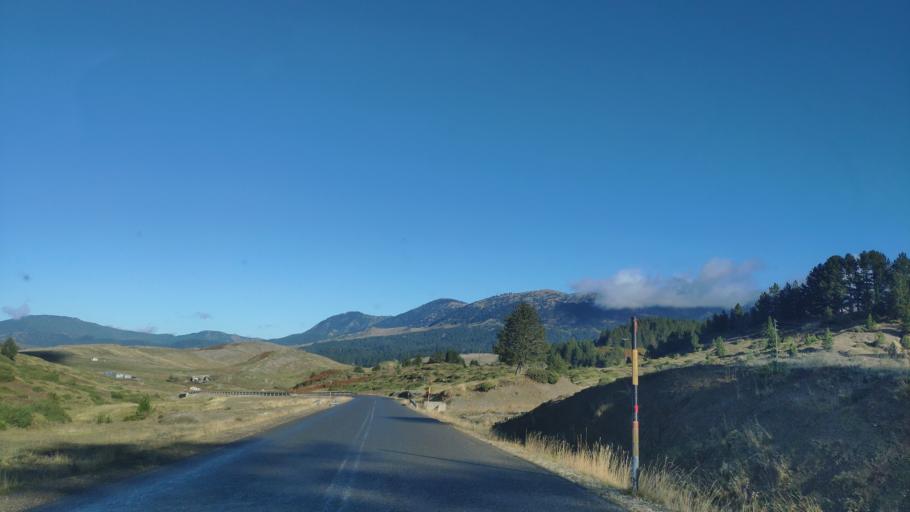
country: GR
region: Epirus
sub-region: Nomos Ioanninon
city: Metsovo
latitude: 39.8030
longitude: 21.1742
